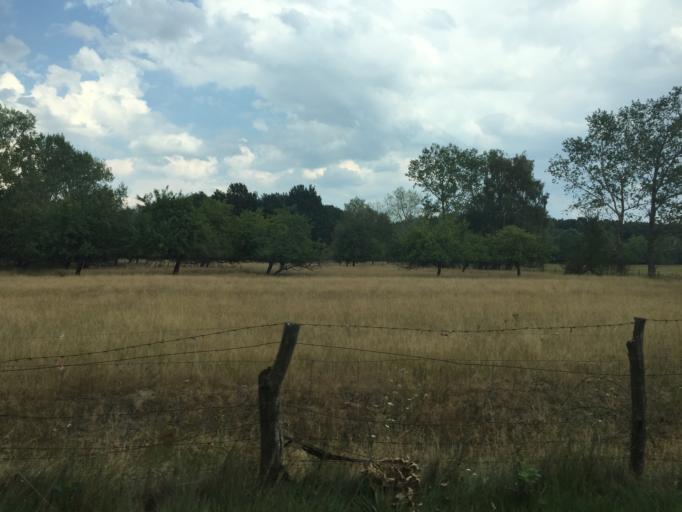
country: DE
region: Saxony
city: Trebendorf
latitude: 51.5233
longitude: 14.5538
